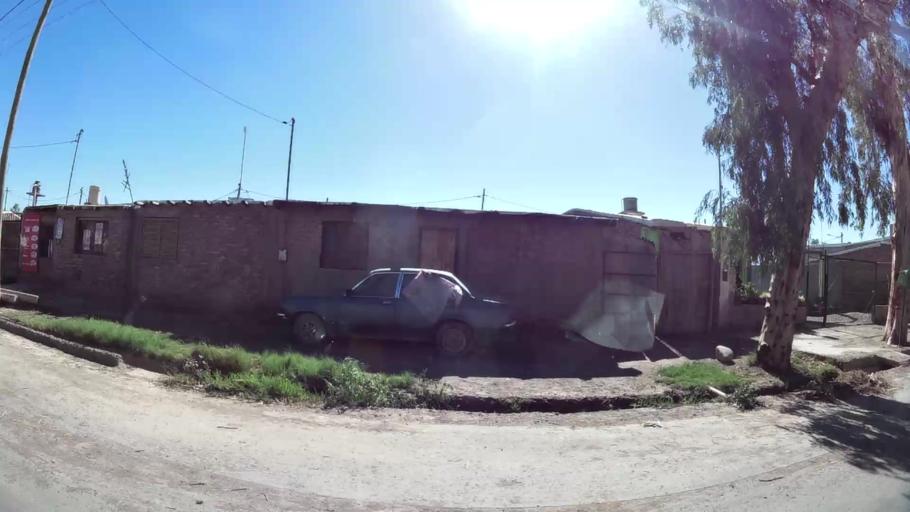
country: AR
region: Mendoza
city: Las Heras
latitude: -32.8304
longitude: -68.8166
